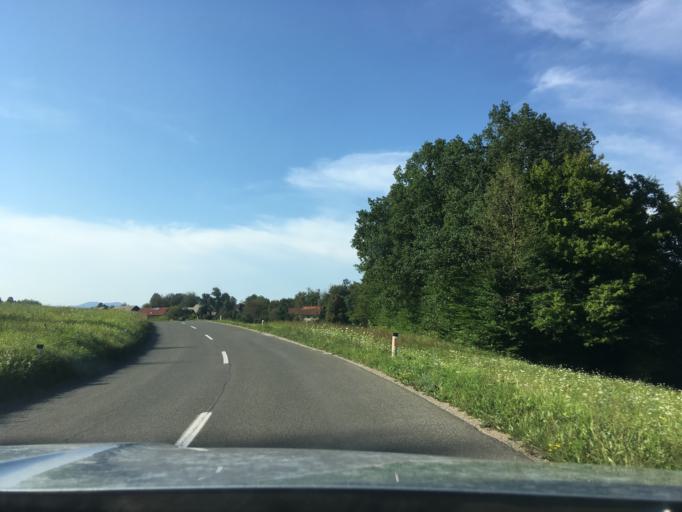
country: SI
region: Crnomelj
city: Crnomelj
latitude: 45.5048
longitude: 15.1900
